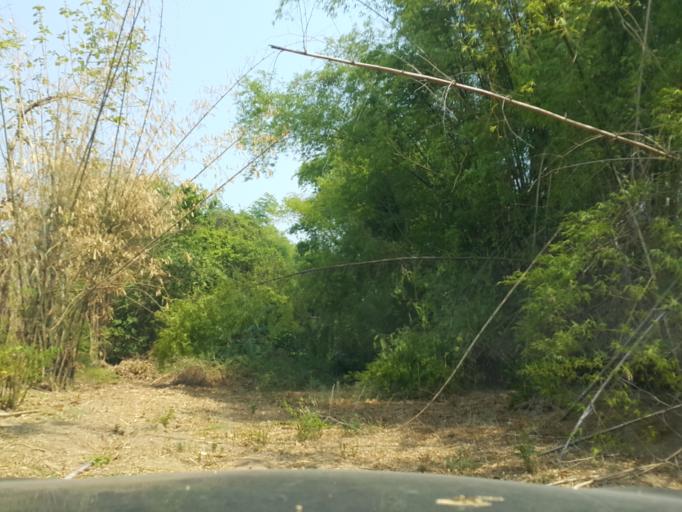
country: TH
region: Sukhothai
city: Thung Saliam
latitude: 17.3149
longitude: 99.5571
